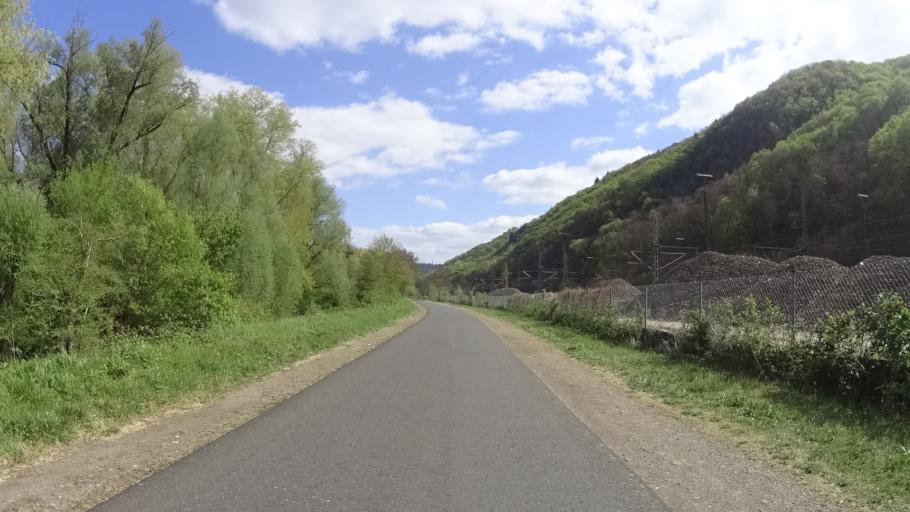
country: DE
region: Rheinland-Pfalz
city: Weiler
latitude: 49.9742
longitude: 7.8682
